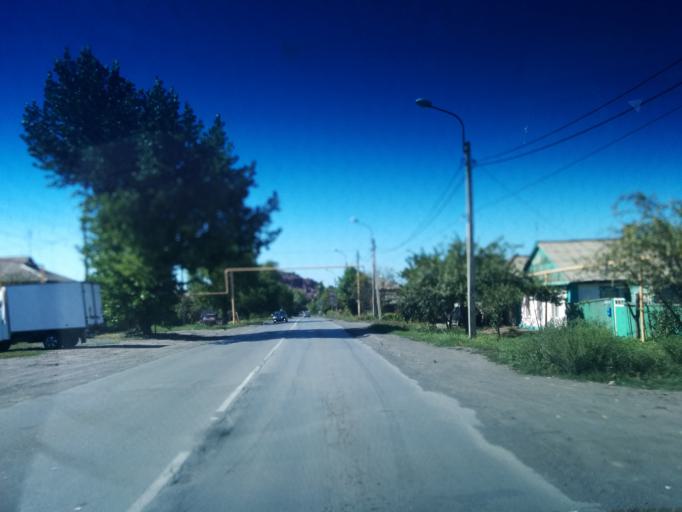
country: RU
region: Rostov
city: Shakhty
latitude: 47.6887
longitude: 40.2636
